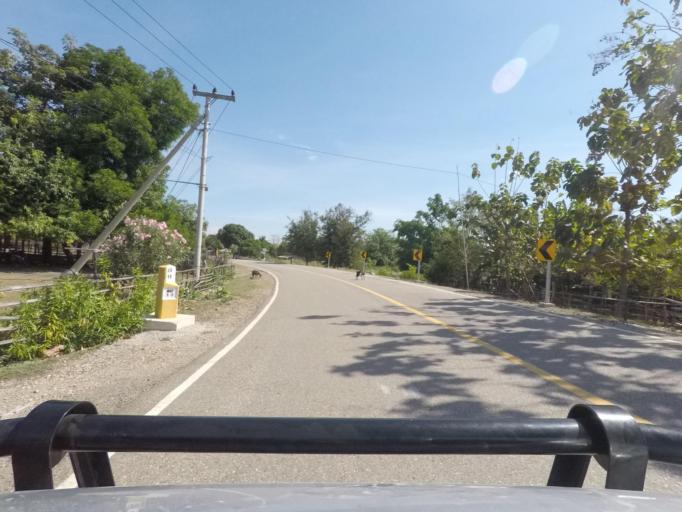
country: TL
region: Bobonaro
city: Maliana
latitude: -8.8680
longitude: 125.0424
